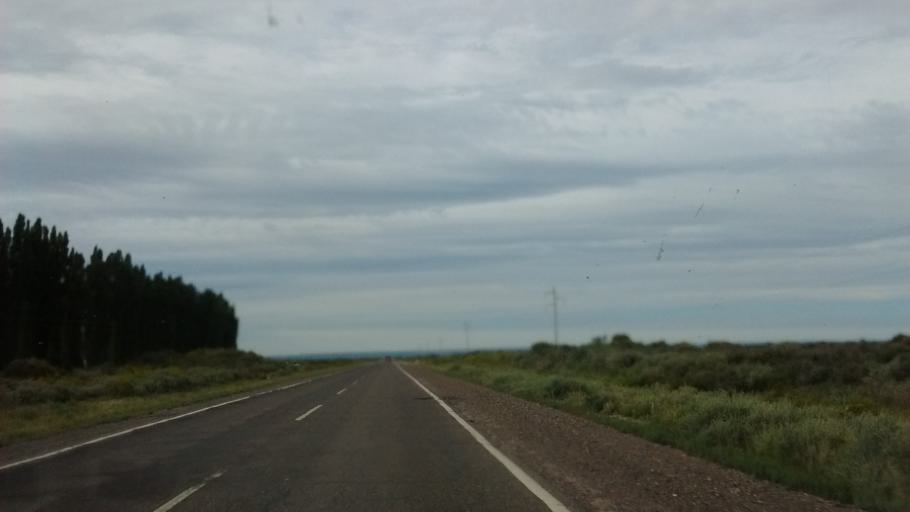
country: AR
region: Rio Negro
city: Catriel
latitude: -37.9388
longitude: -67.8839
